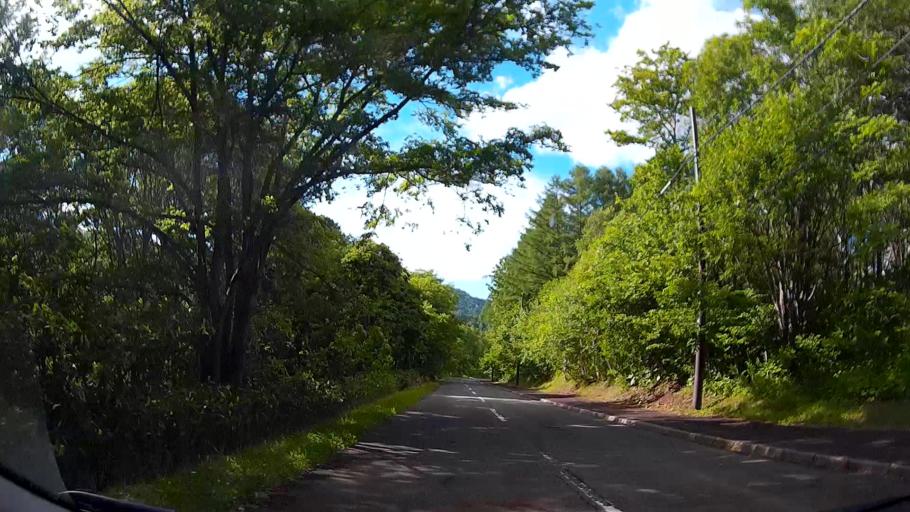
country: JP
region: Hokkaido
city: Sapporo
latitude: 42.9405
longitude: 141.1542
